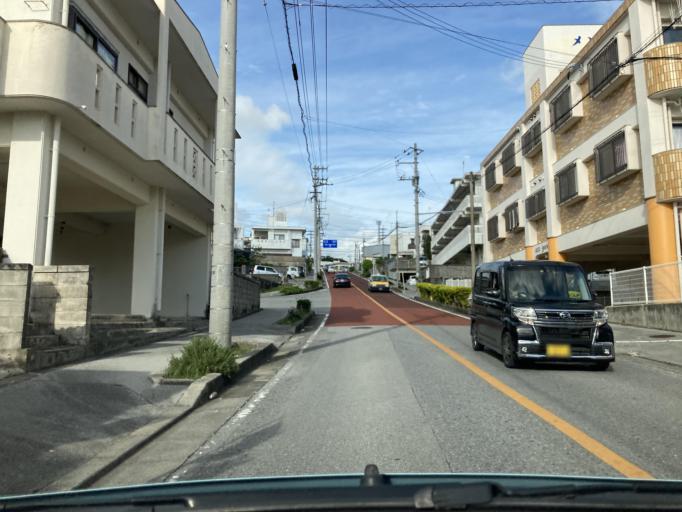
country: JP
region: Okinawa
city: Itoman
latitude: 26.1284
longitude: 127.6781
